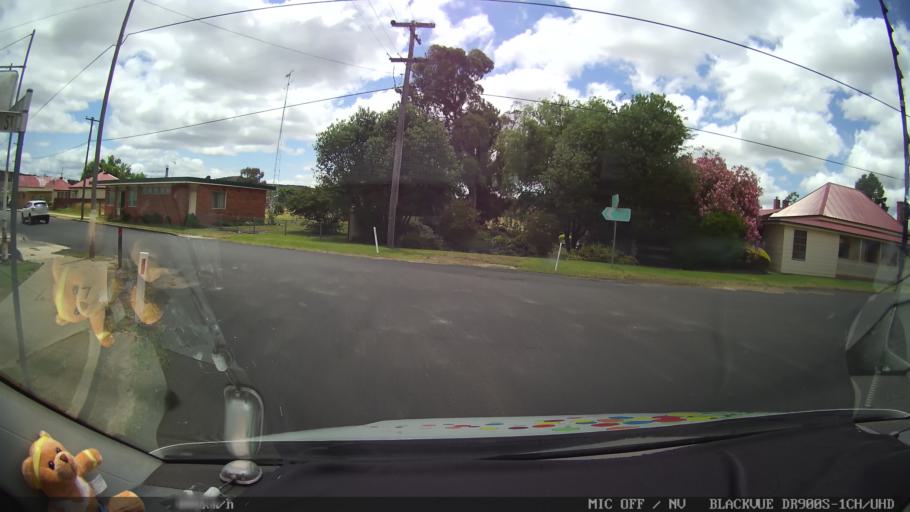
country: AU
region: New South Wales
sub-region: Glen Innes Severn
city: Glen Innes
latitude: -29.4446
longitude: 151.5989
